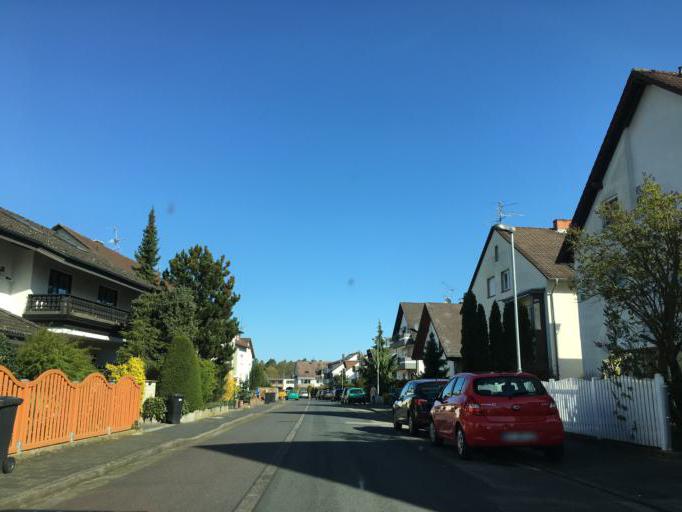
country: DE
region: Hesse
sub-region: Regierungsbezirk Darmstadt
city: Muehlheim am Main
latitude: 50.0999
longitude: 8.8550
